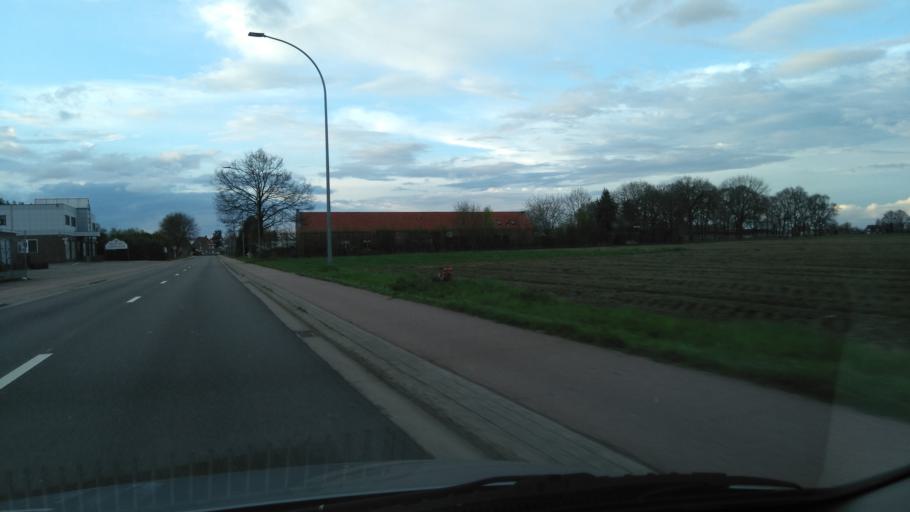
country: BE
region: Flanders
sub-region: Provincie Antwerpen
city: Geel
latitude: 51.1325
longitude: 4.9805
